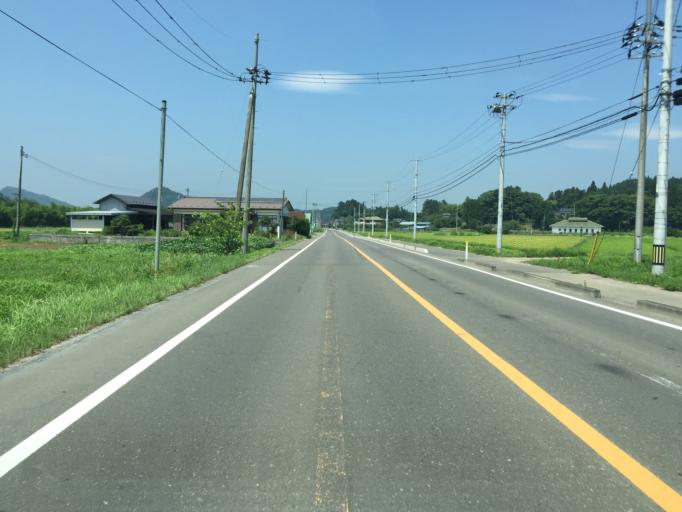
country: JP
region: Miyagi
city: Marumori
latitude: 37.8805
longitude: 140.8210
